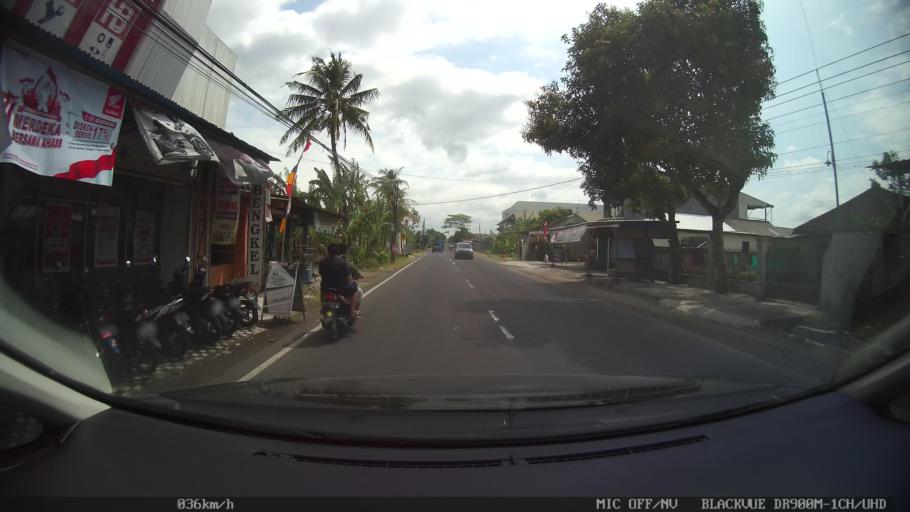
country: ID
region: Daerah Istimewa Yogyakarta
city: Depok
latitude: -7.8342
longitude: 110.4771
